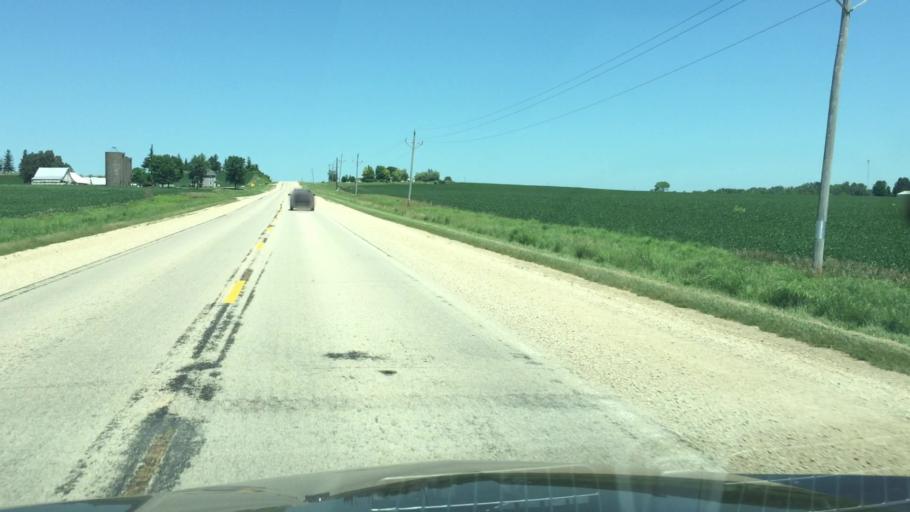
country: US
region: Iowa
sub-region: Cedar County
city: Mechanicsville
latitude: 41.9766
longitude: -91.1417
